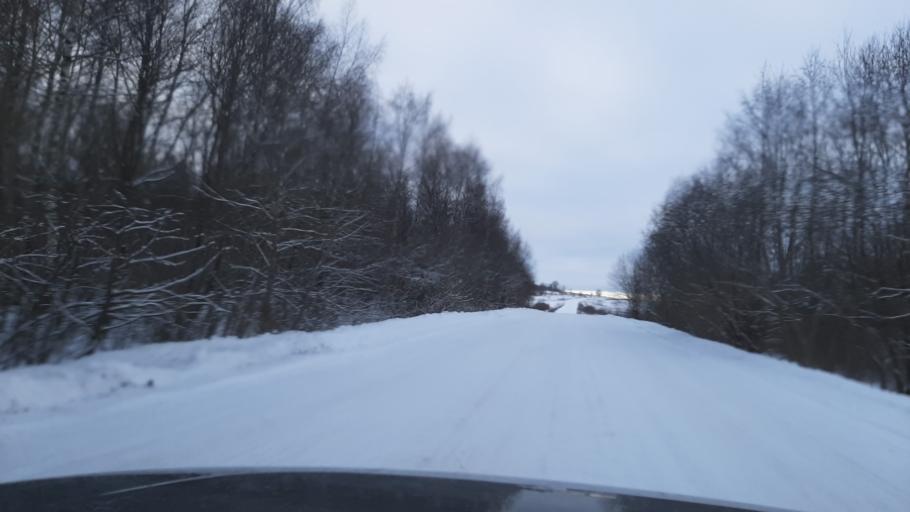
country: RU
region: Kostroma
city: Volgorechensk
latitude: 57.4447
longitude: 40.9505
